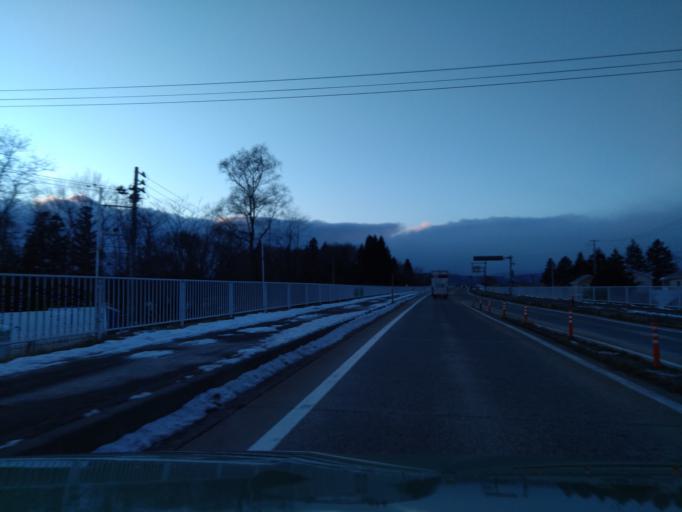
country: JP
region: Iwate
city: Shizukuishi
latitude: 39.6898
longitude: 140.9907
